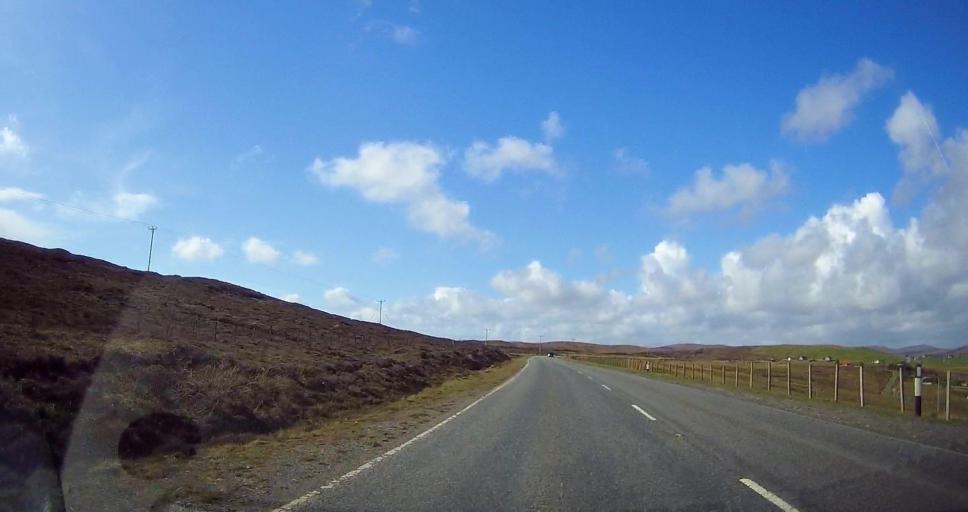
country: GB
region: Scotland
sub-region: Shetland Islands
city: Lerwick
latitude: 60.2261
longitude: -1.2355
